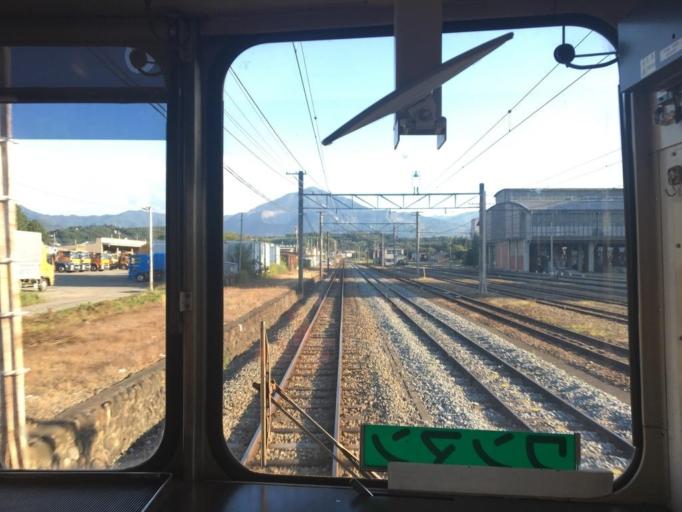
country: JP
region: Saitama
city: Chichibu
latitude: 36.0288
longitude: 139.0971
